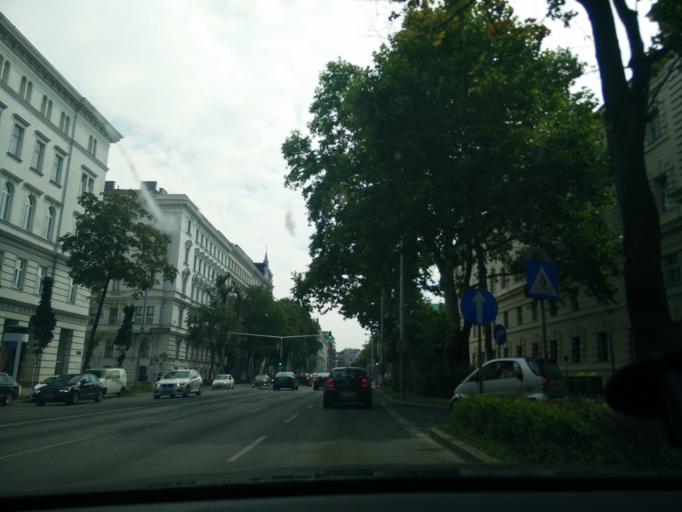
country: AT
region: Vienna
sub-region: Wien Stadt
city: Vienna
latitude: 48.2134
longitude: 16.3558
